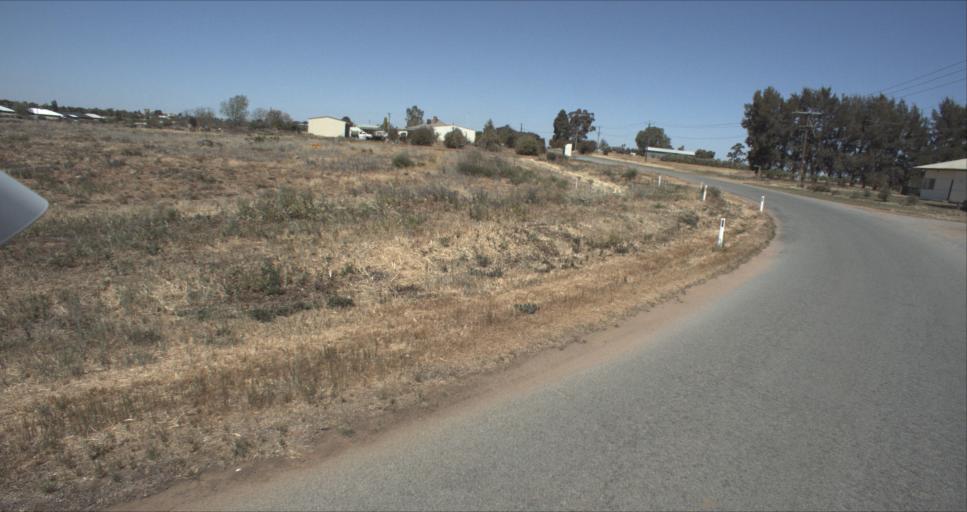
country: AU
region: New South Wales
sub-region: Leeton
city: Leeton
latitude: -34.5371
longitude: 146.3958
